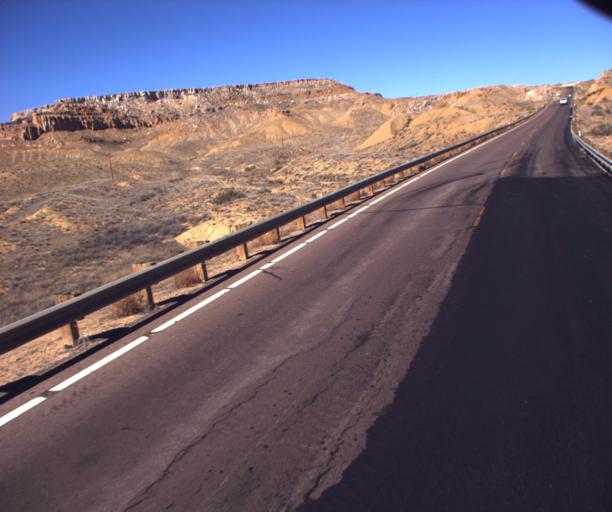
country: US
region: Arizona
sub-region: Navajo County
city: First Mesa
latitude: 35.7973
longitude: -110.5129
